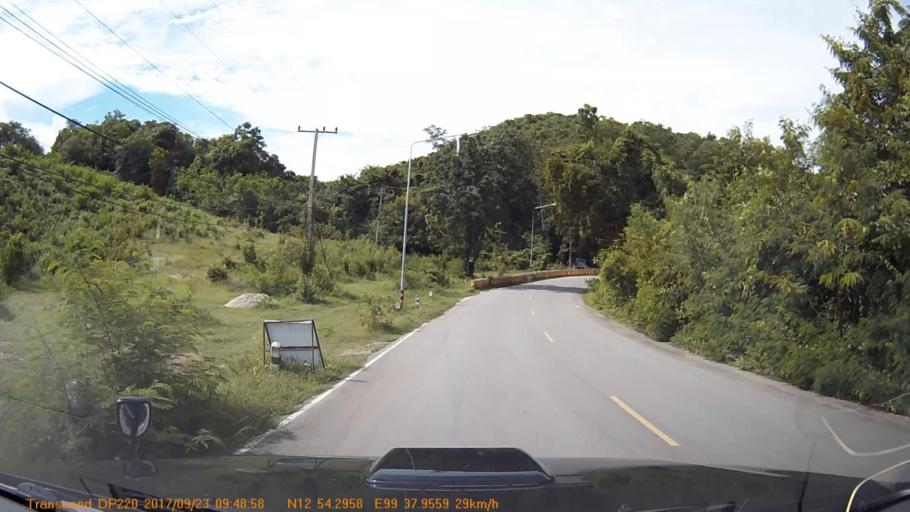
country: TH
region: Phetchaburi
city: Kaeng Krachan
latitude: 12.9050
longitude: 99.6325
